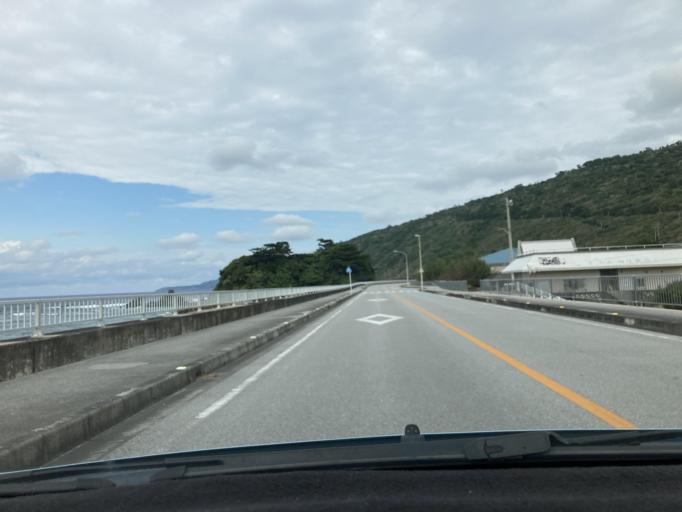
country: JP
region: Okinawa
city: Nago
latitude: 26.7860
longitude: 128.2197
